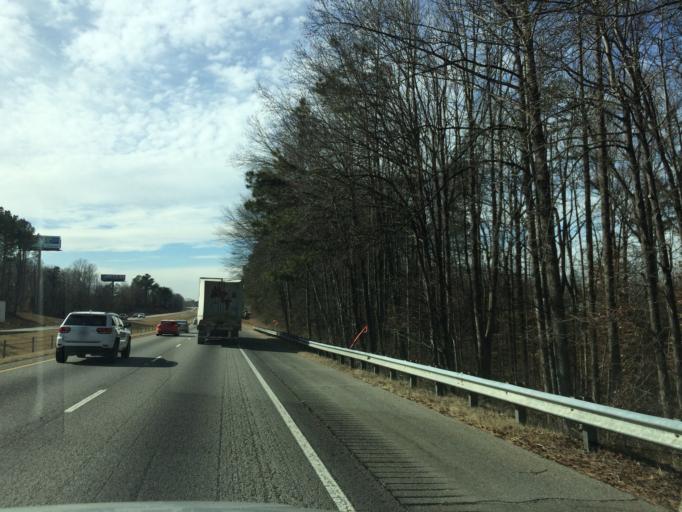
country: US
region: Georgia
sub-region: Jackson County
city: Braselton
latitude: 34.1226
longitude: -83.7487
